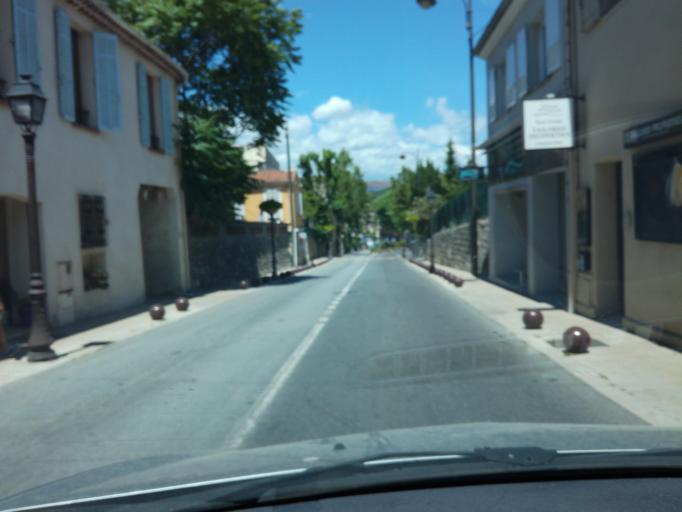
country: FR
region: Provence-Alpes-Cote d'Azur
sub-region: Departement des Alpes-Maritimes
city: Mougins
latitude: 43.5992
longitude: 6.9862
